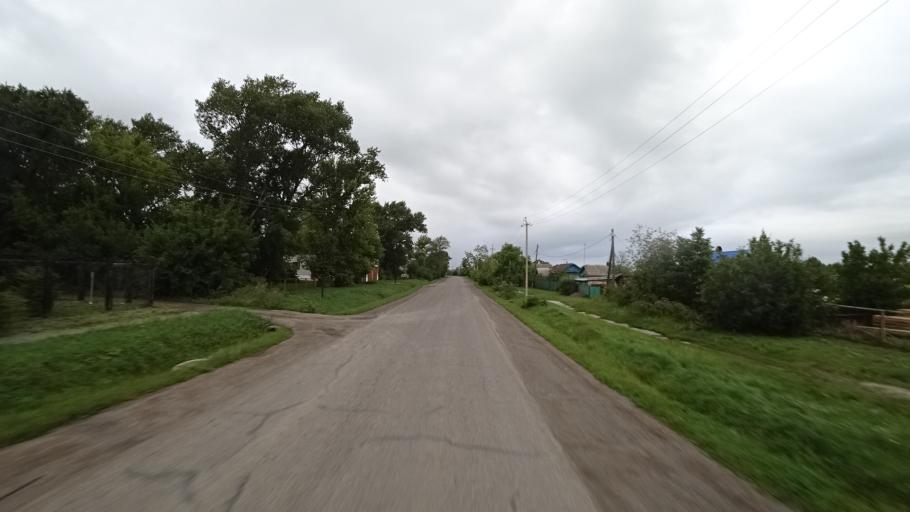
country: RU
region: Primorskiy
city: Chernigovka
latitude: 44.3435
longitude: 132.5799
